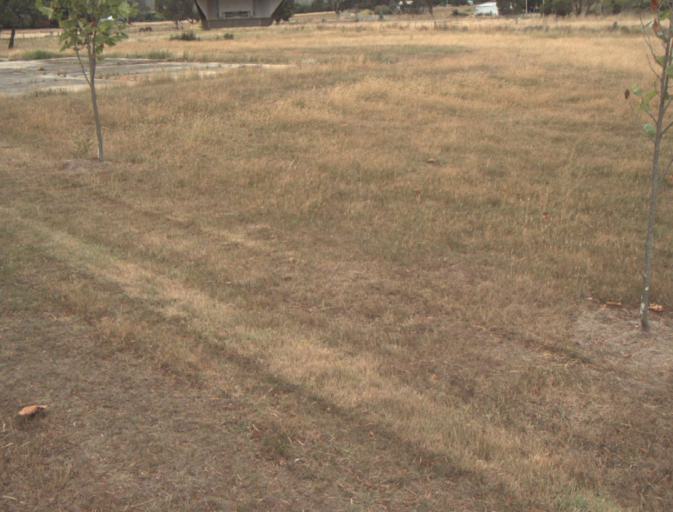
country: AU
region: Tasmania
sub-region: Launceston
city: Mayfield
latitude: -41.2954
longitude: 146.9847
